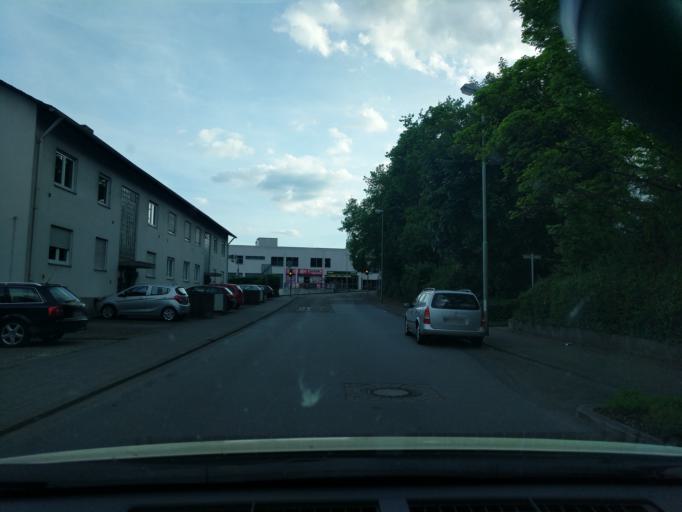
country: DE
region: Rheinland-Pfalz
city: Kaiserslautern
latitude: 49.4452
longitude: 7.7347
